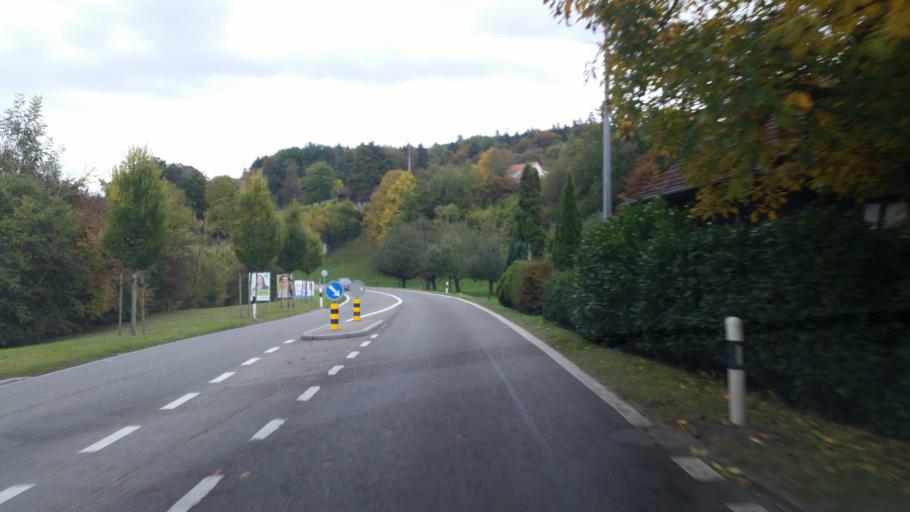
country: CH
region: Aargau
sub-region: Bezirk Zurzach
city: Oberendingen
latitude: 47.5365
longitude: 8.2909
